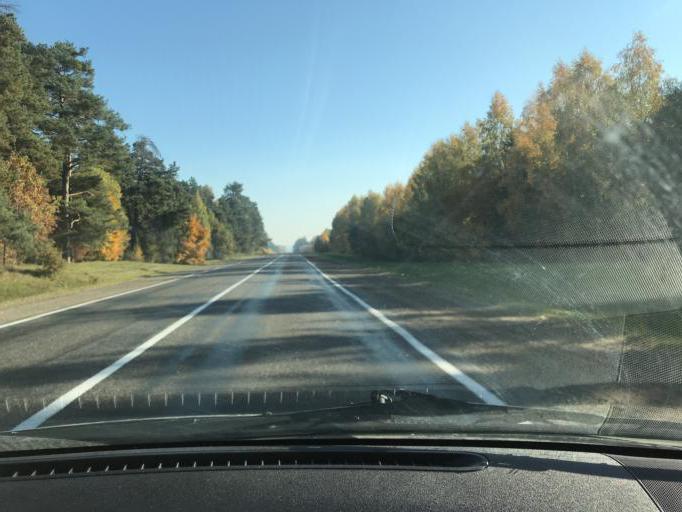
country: BY
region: Brest
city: Lyakhavichy
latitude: 52.9612
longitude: 26.4231
